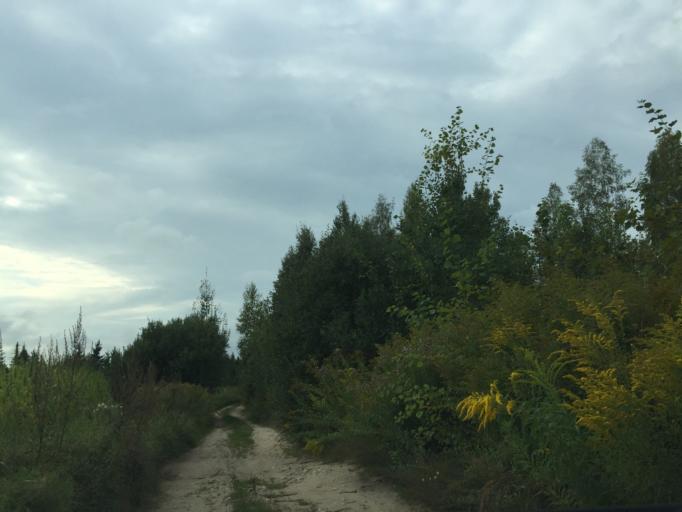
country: LV
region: Baldone
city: Baldone
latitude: 56.7655
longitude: 24.4634
